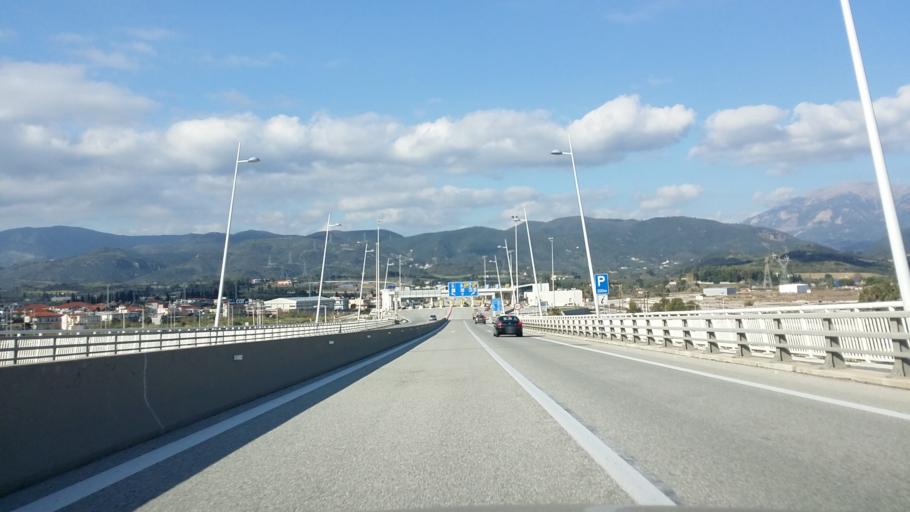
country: GR
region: West Greece
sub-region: Nomos Aitolias kai Akarnanias
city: Antirrio
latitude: 38.3302
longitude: 21.7680
